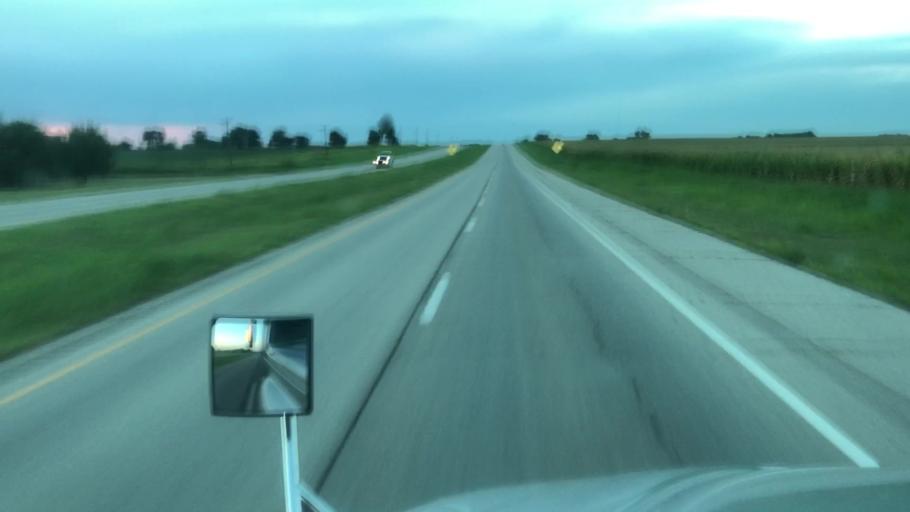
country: US
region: Oklahoma
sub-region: Kay County
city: Newkirk
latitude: 36.7980
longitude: -97.0673
